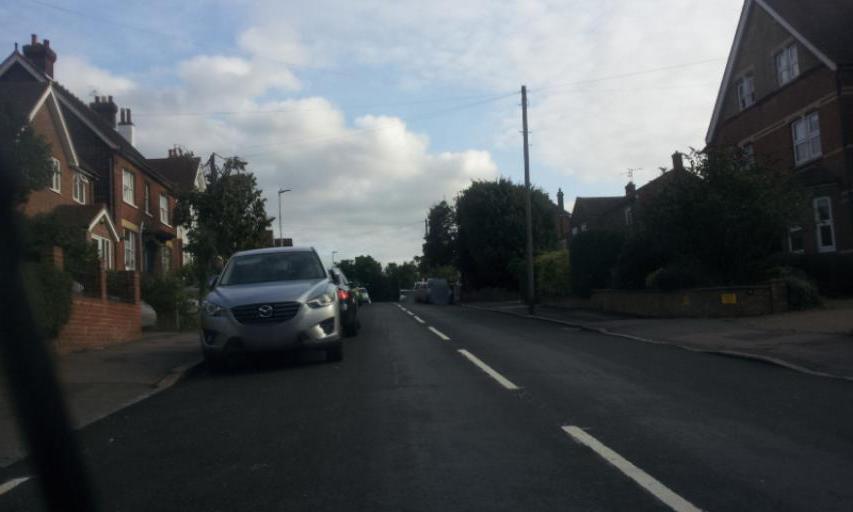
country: GB
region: England
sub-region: Kent
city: Tonbridge
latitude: 51.1870
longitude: 0.2788
